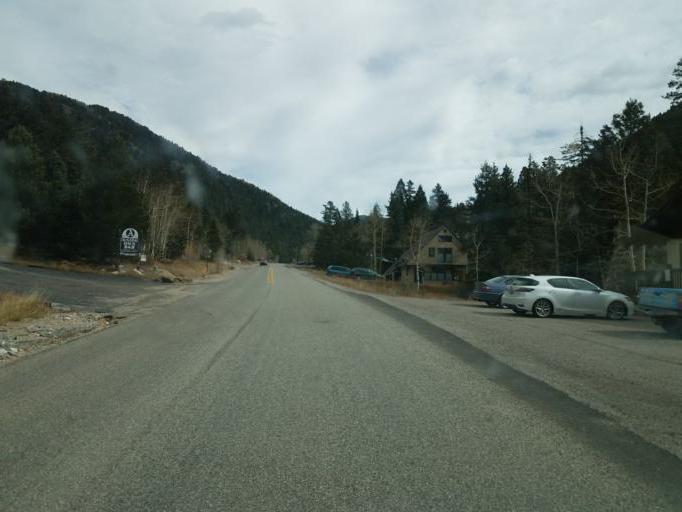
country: US
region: New Mexico
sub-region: Taos County
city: Arroyo Seco
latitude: 36.5935
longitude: -105.4834
